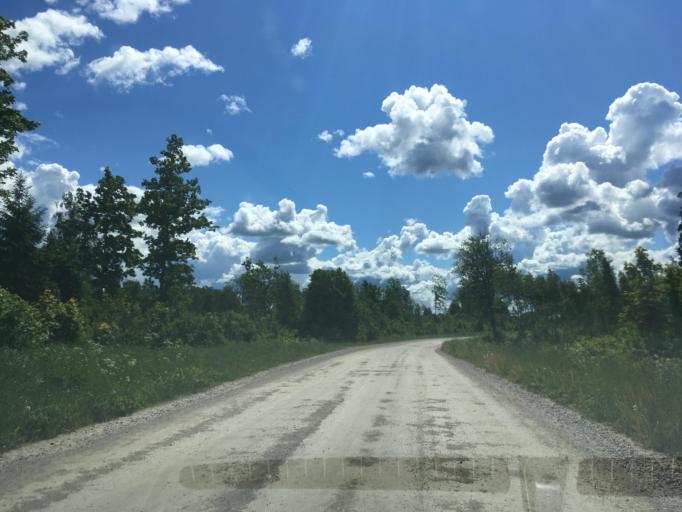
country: EE
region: Harju
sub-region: Nissi vald
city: Turba
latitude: 58.9322
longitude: 24.1519
